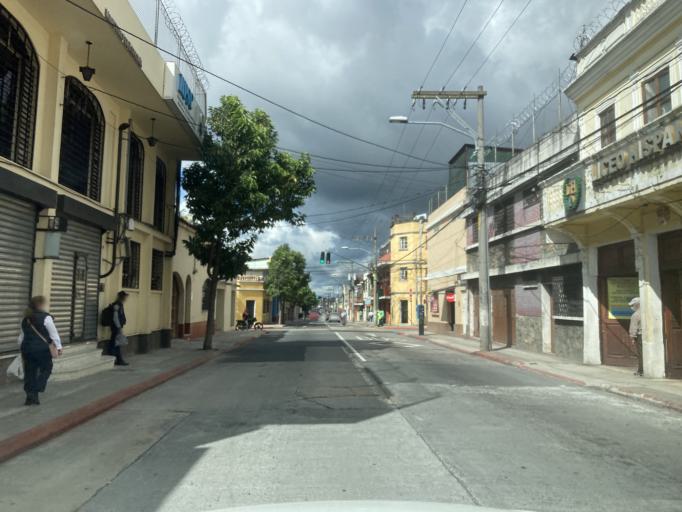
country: GT
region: Guatemala
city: Guatemala City
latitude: 14.6445
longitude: -90.5077
